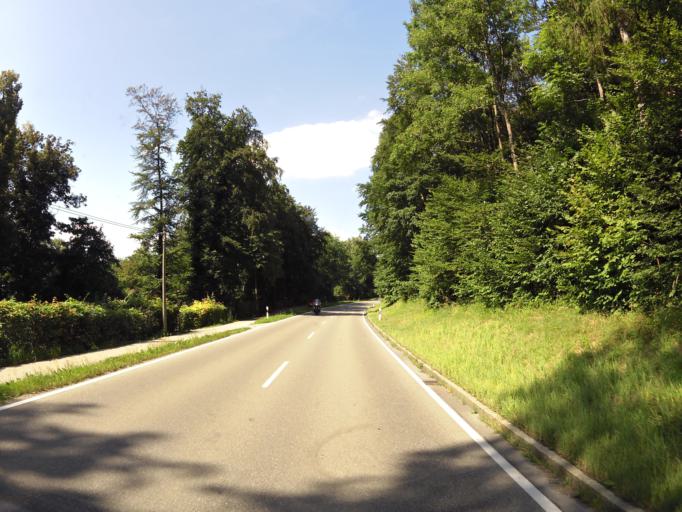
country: DE
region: Bavaria
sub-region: Upper Bavaria
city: Andechs
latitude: 47.9661
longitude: 11.1511
